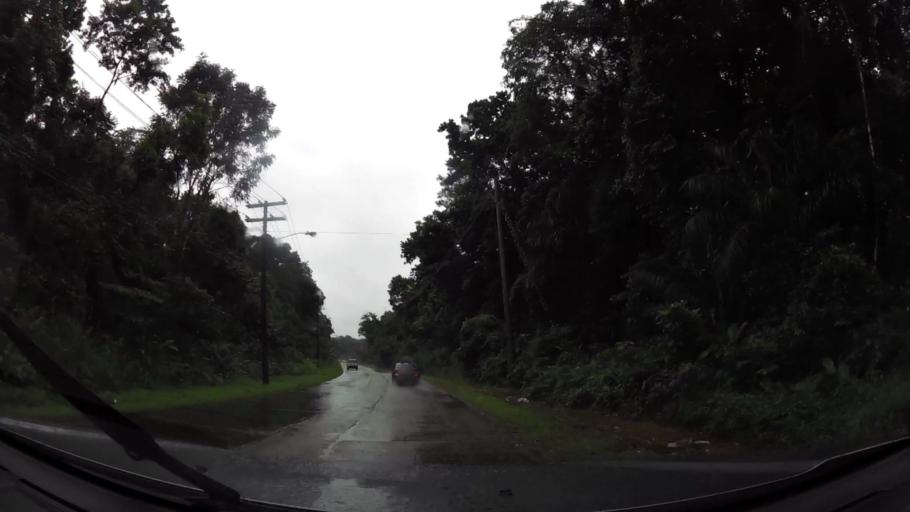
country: PA
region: Colon
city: Las Margaritas
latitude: 9.3226
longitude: -79.8890
